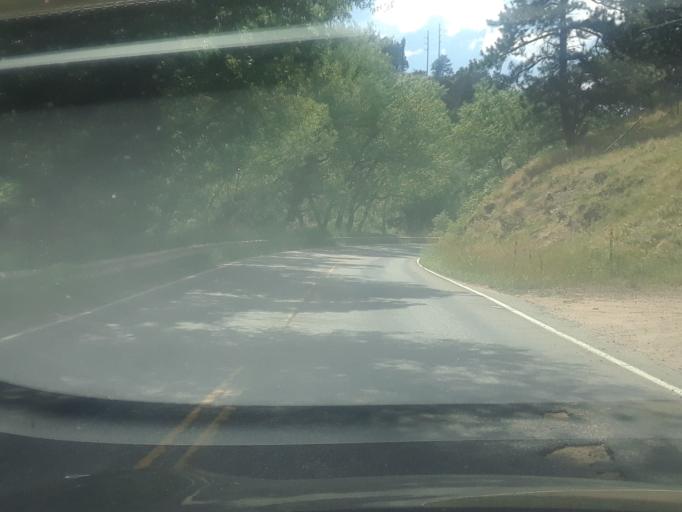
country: US
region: Colorado
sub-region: Boulder County
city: Boulder
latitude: 40.0257
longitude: -105.3100
